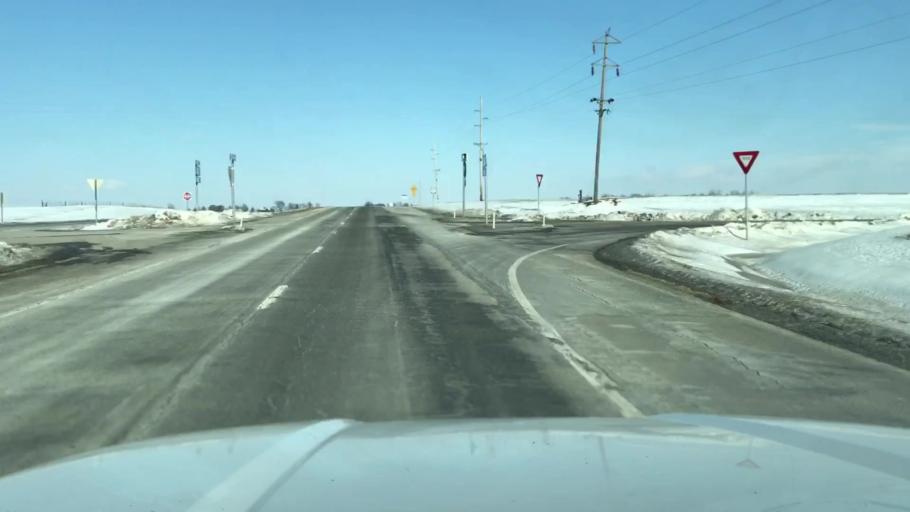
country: US
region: Missouri
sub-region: Nodaway County
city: Maryville
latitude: 40.2582
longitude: -94.8668
